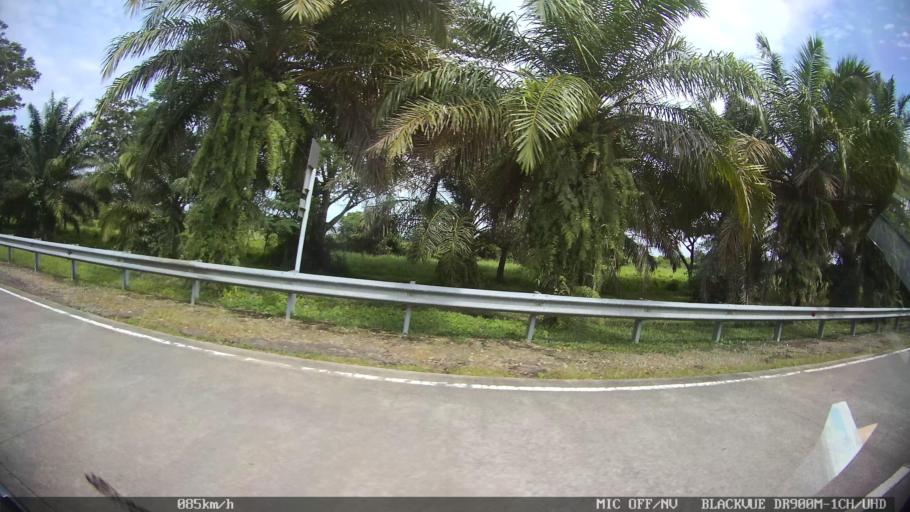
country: ID
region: North Sumatra
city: Percut
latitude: 3.6218
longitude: 98.8651
